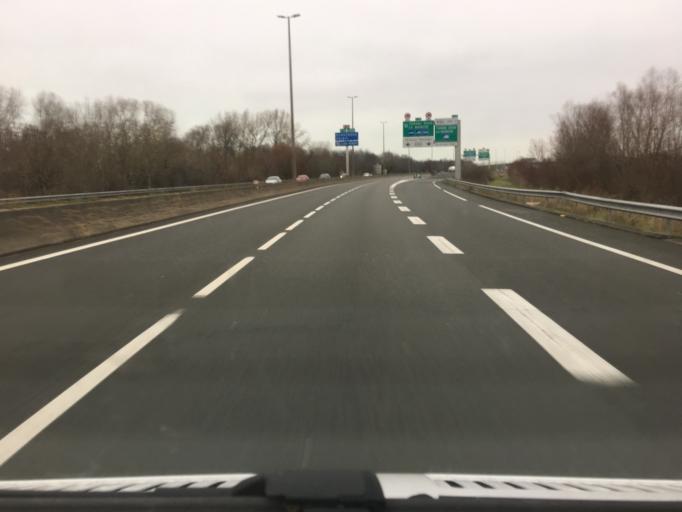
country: FR
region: Nord-Pas-de-Calais
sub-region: Departement du Pas-de-Calais
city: Coquelles
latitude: 50.9373
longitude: 1.8059
